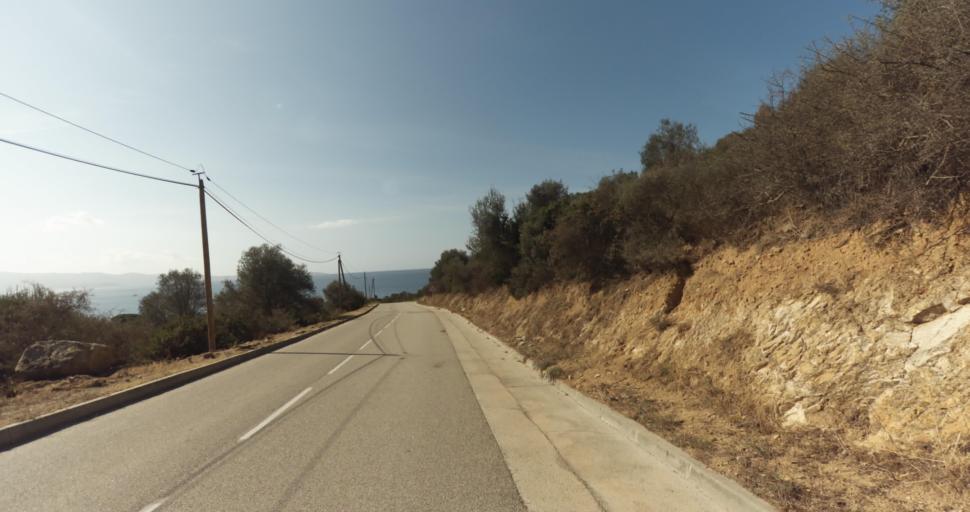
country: FR
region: Corsica
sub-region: Departement de la Corse-du-Sud
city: Ajaccio
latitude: 41.9141
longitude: 8.6438
